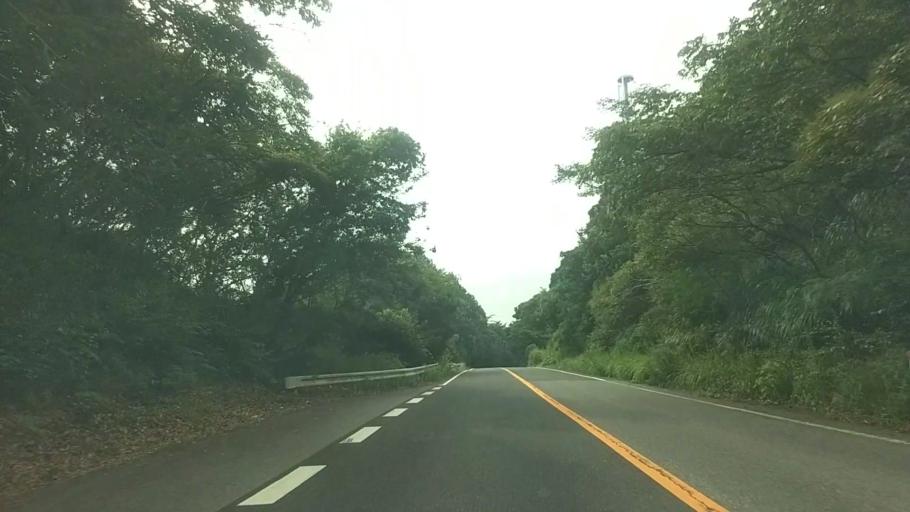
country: JP
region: Chiba
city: Kimitsu
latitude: 35.2341
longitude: 140.0108
